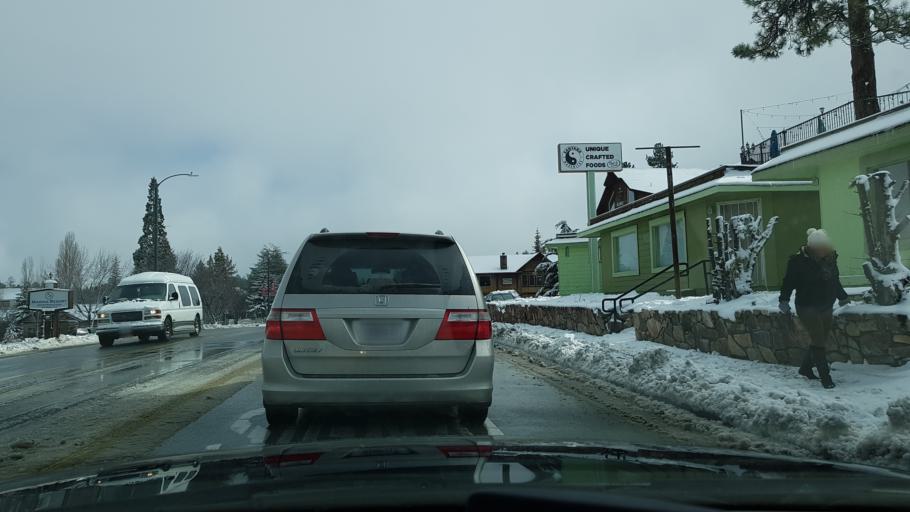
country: US
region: California
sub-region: San Bernardino County
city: Big Bear Lake
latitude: 34.2437
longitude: -116.9131
